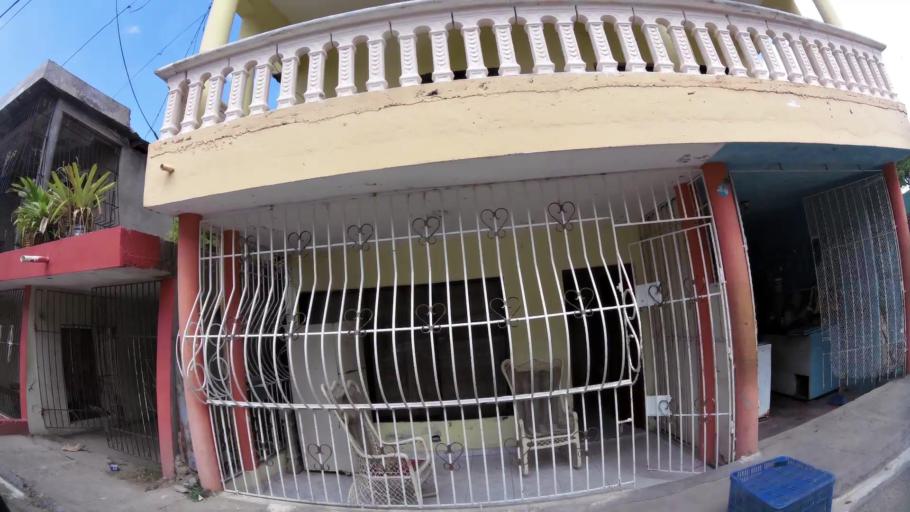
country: DO
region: San Cristobal
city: San Cristobal
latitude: 18.4270
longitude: -70.1153
